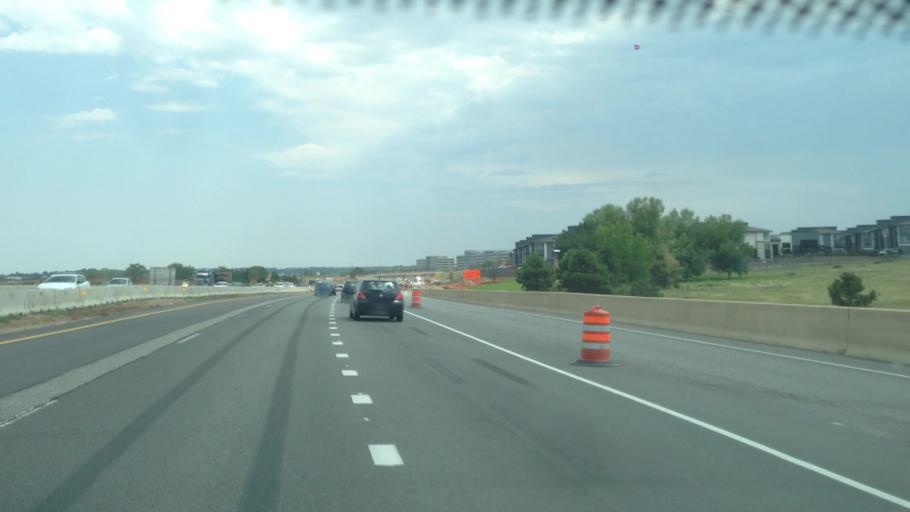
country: US
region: Colorado
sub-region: Arapahoe County
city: Columbine Valley
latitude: 39.5634
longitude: -105.0200
